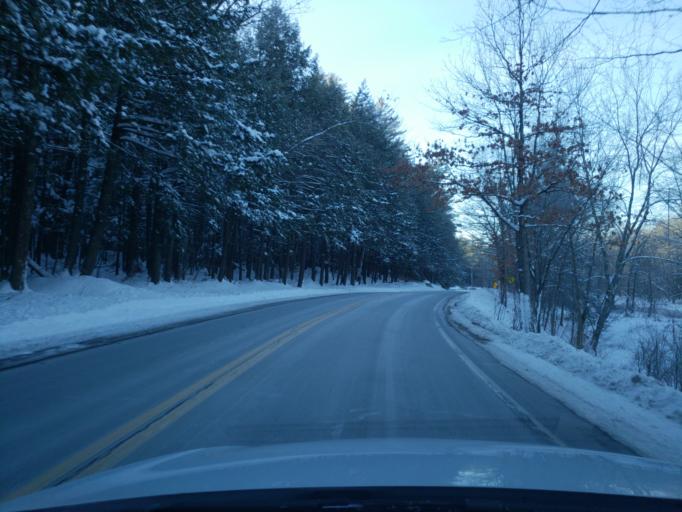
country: US
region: New Hampshire
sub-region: Hillsborough County
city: Goffstown
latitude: 43.0090
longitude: -71.6464
